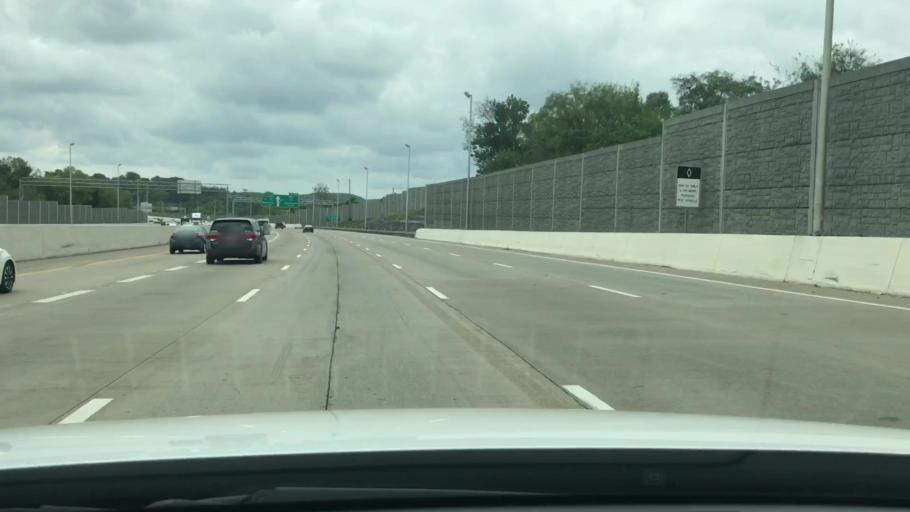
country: US
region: Tennessee
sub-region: Davidson County
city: Nashville
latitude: 36.2360
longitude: -86.7655
